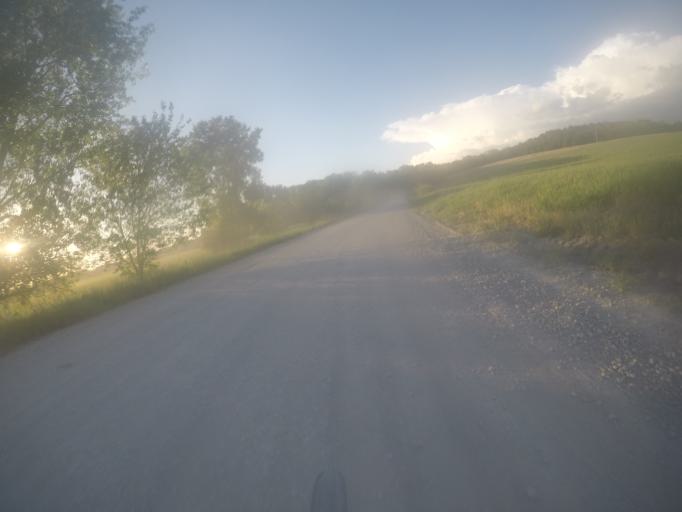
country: US
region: Kansas
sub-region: Riley County
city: Manhattan
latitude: 39.2296
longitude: -96.5479
